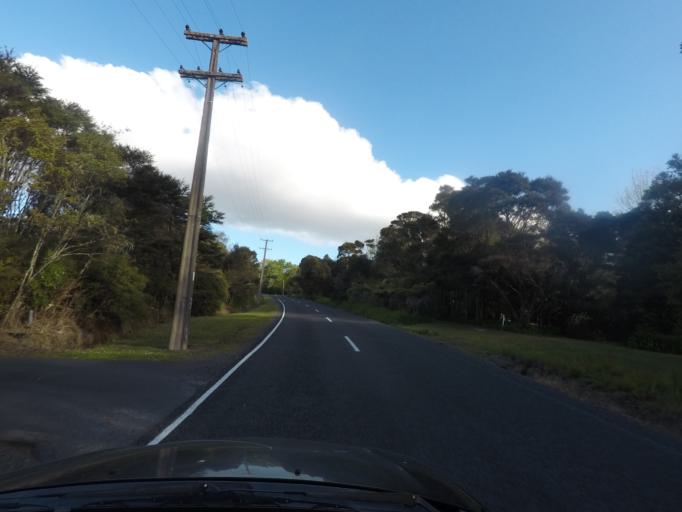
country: NZ
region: Auckland
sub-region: Auckland
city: Waitakere
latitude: -36.9222
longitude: 174.6155
